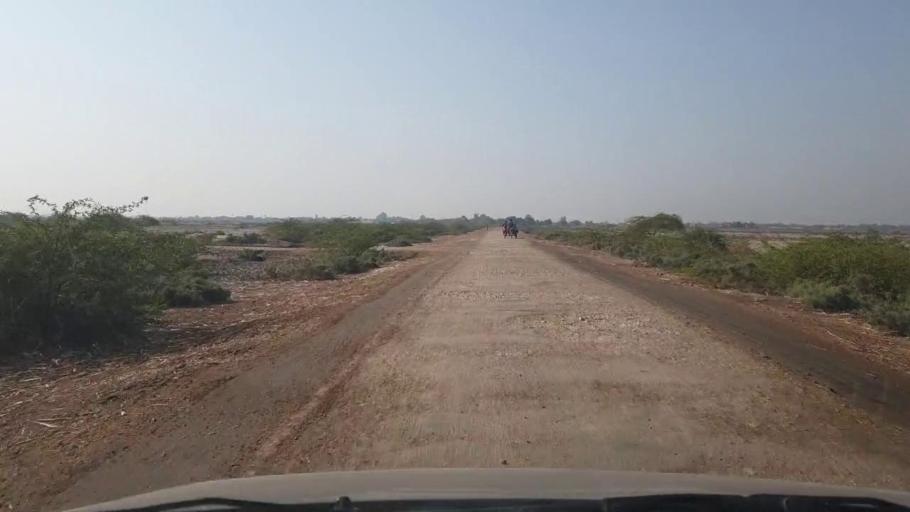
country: PK
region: Sindh
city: Mirwah Gorchani
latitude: 25.2868
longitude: 69.1415
